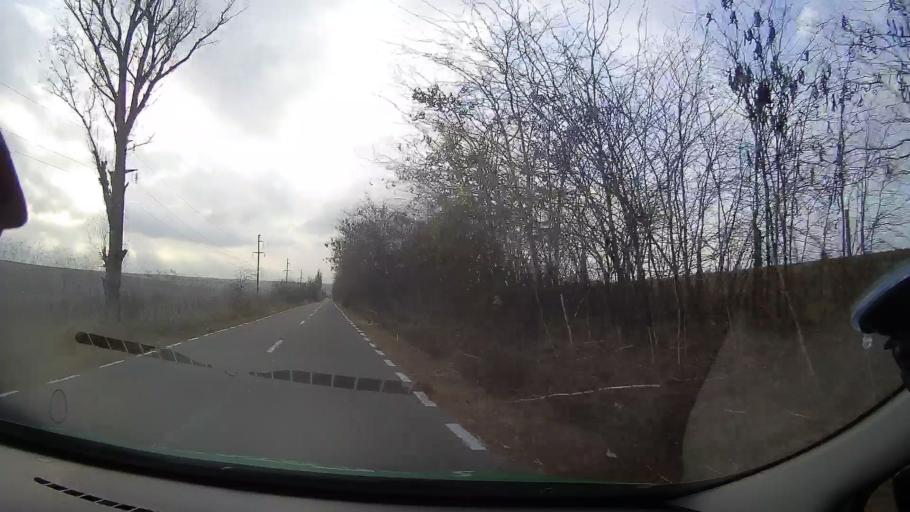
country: RO
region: Constanta
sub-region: Comuna Mircea Voda
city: Satu Nou
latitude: 44.2370
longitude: 28.2420
